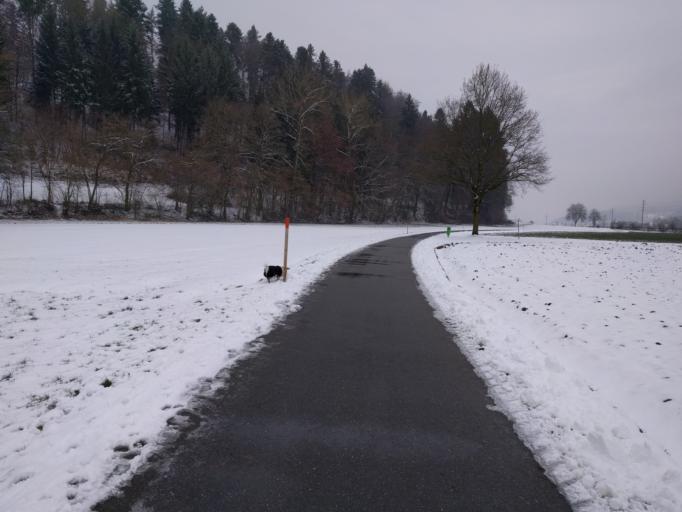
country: CH
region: Aargau
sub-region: Bezirk Kulm
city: Schoftland
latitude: 47.3112
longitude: 8.0430
